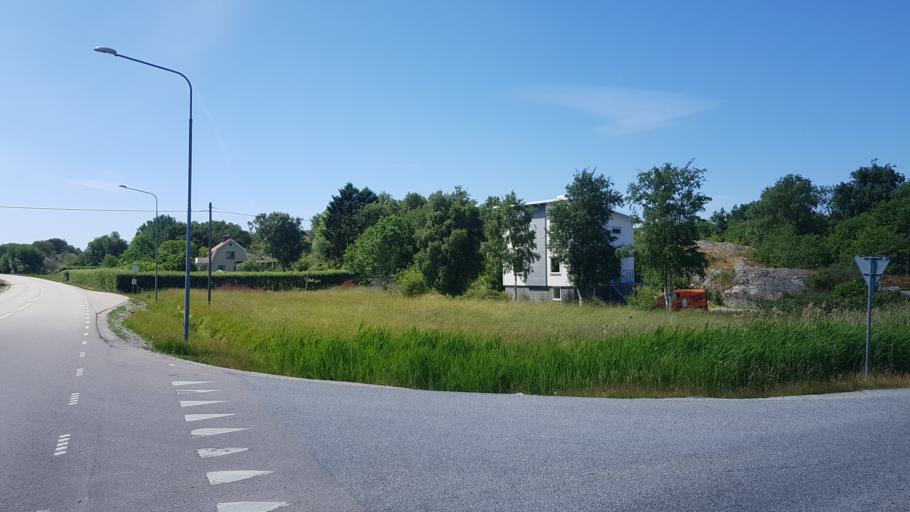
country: SE
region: Vaestra Goetaland
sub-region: Tjorns Kommun
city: Skaerhamn
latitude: 57.9879
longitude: 11.5719
